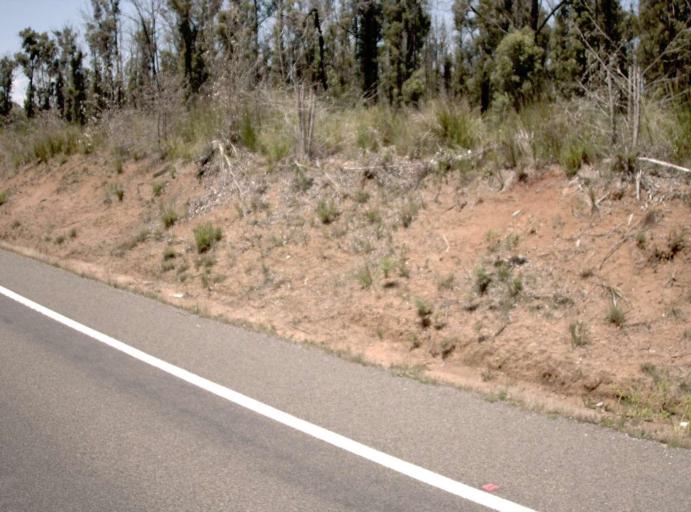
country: AU
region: Victoria
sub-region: East Gippsland
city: Lakes Entrance
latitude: -37.7490
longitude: 148.2233
